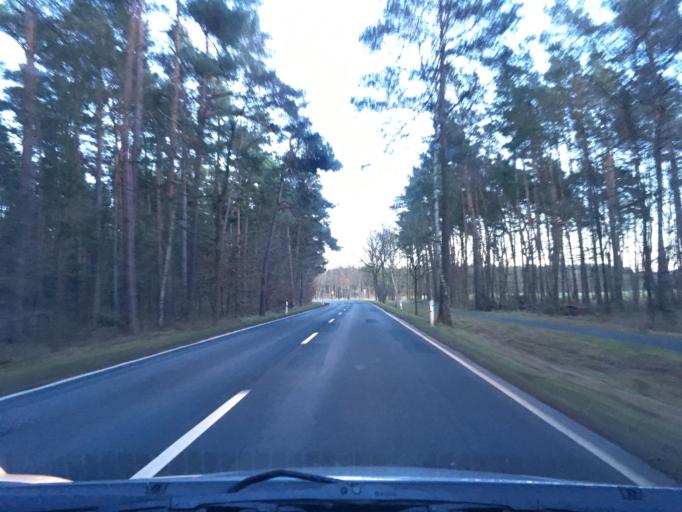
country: DE
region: Lower Saxony
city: Kusten
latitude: 52.9816
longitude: 11.0166
